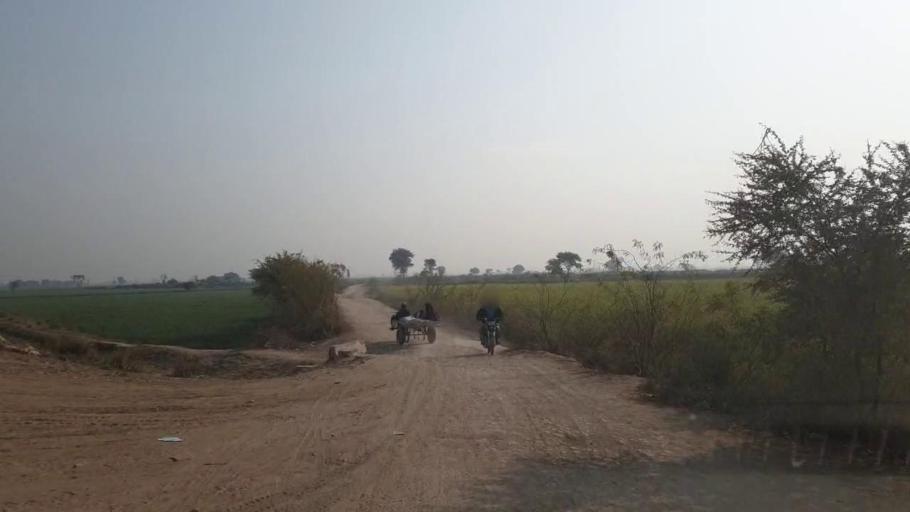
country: PK
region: Sindh
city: Hala
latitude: 25.7712
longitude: 68.3872
